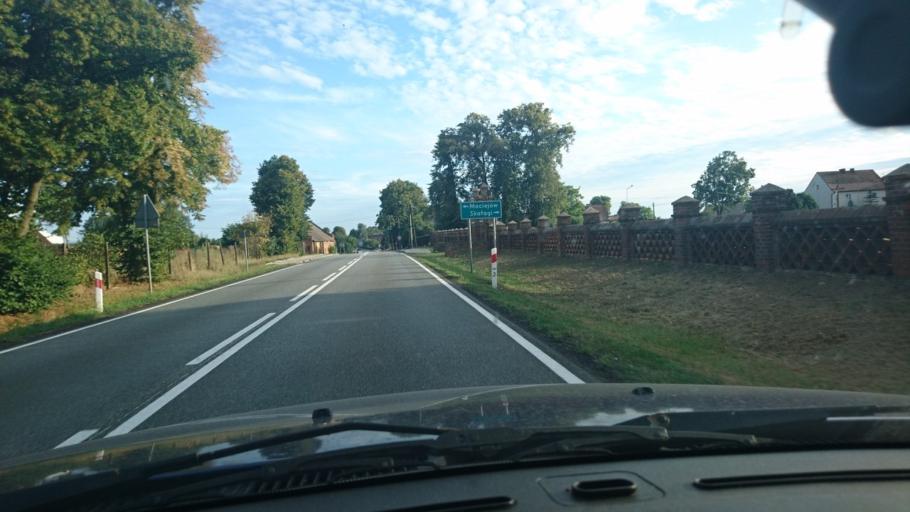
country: PL
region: Opole Voivodeship
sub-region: Powiat kluczborski
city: Kluczbork
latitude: 51.0307
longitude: 18.1924
